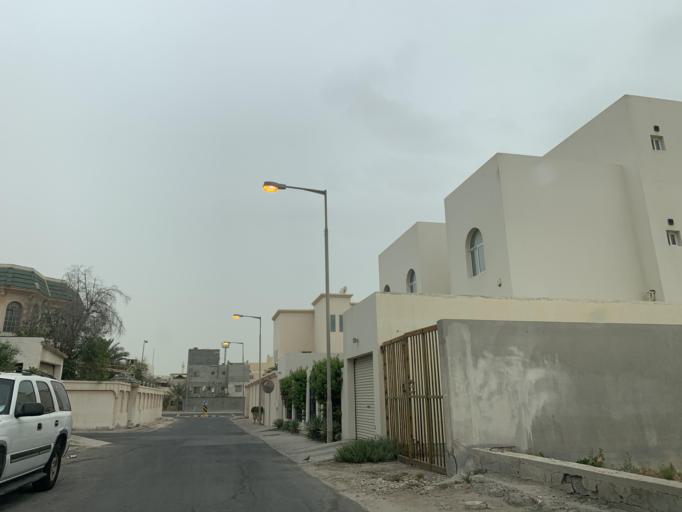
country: BH
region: Central Governorate
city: Madinat Hamad
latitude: 26.1470
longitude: 50.5222
